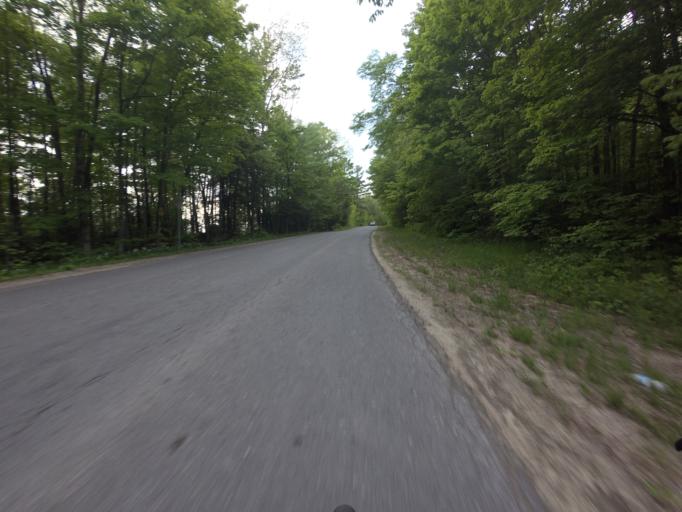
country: US
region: New York
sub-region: St. Lawrence County
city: Gouverneur
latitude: 44.1474
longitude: -75.3524
